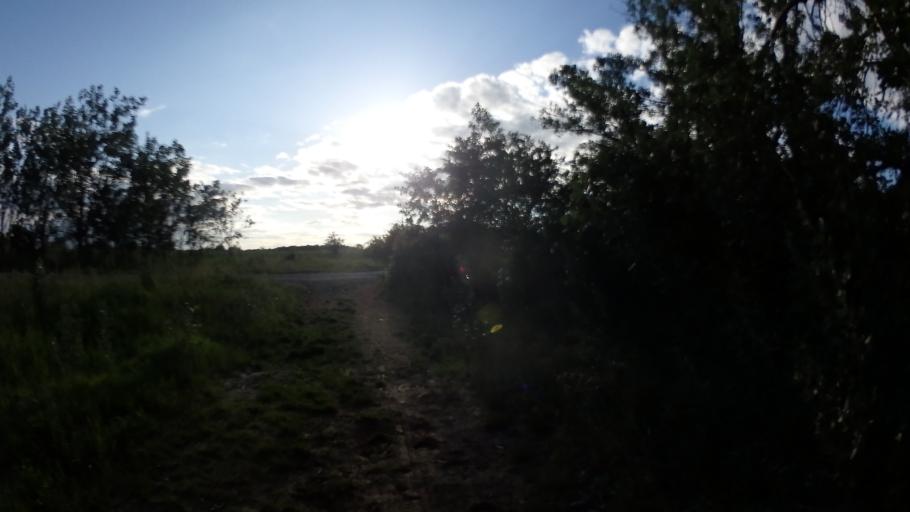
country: CZ
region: South Moravian
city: Ostopovice
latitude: 49.1492
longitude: 16.5487
